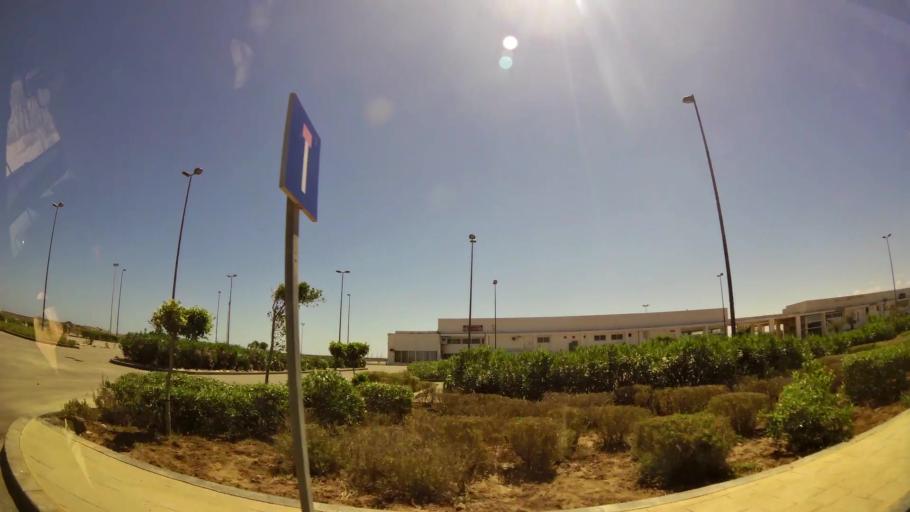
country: MA
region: Oriental
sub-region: Berkane-Taourirt
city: Madagh
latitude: 35.1117
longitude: -2.2991
